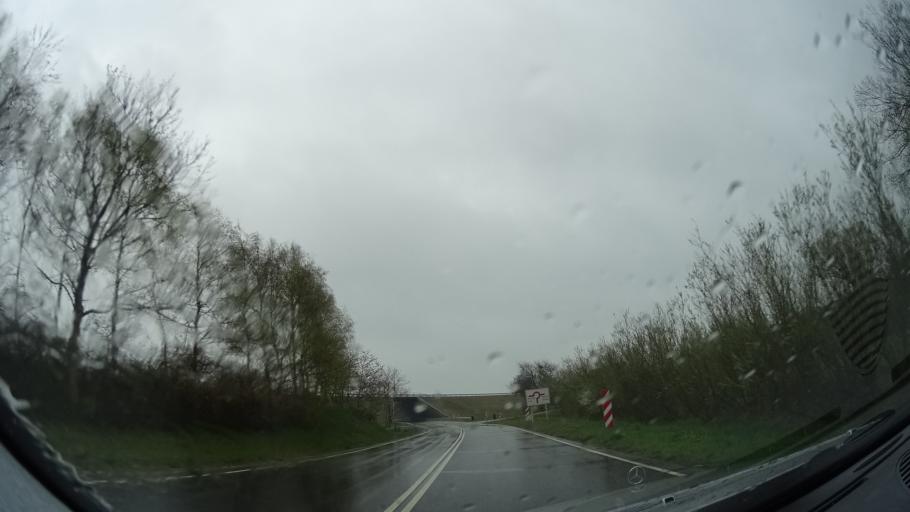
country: DK
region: Zealand
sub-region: Odsherred Kommune
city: Asnaes
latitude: 55.8169
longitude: 11.5821
